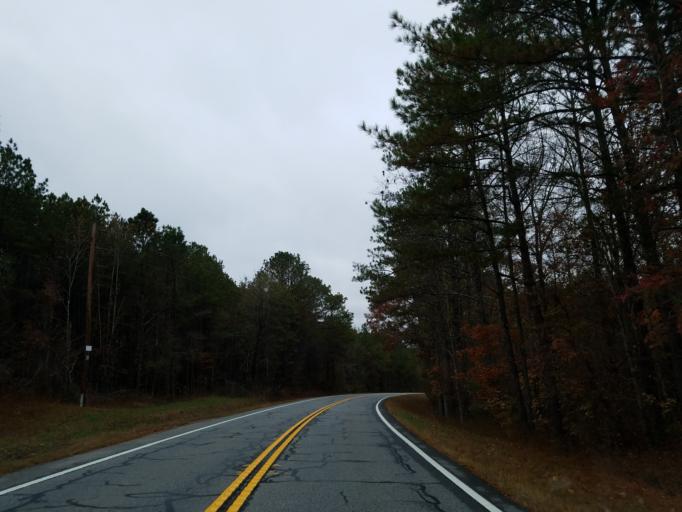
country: US
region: Georgia
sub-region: Cherokee County
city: Canton
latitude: 34.2597
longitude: -84.5996
